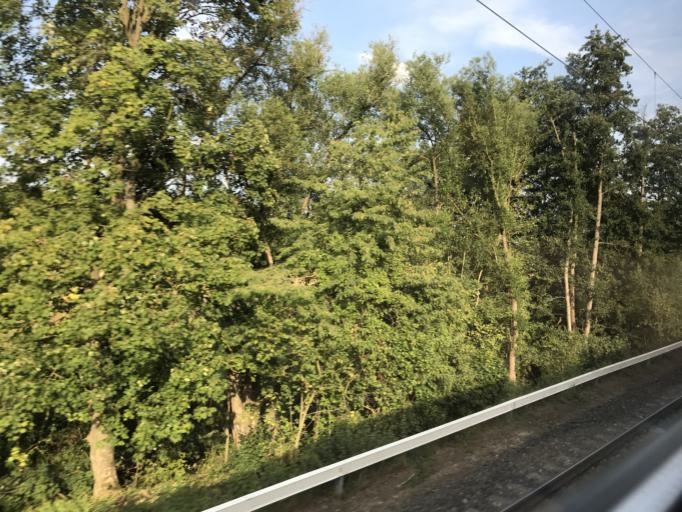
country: DE
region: Hesse
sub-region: Regierungsbezirk Giessen
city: Villmar
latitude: 50.3410
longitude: 8.2132
